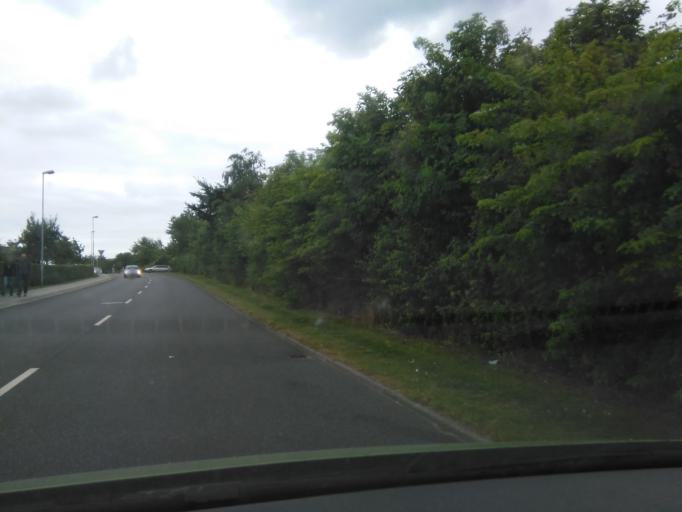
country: DK
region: Central Jutland
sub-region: Arhus Kommune
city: Beder
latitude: 56.0559
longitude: 10.2031
